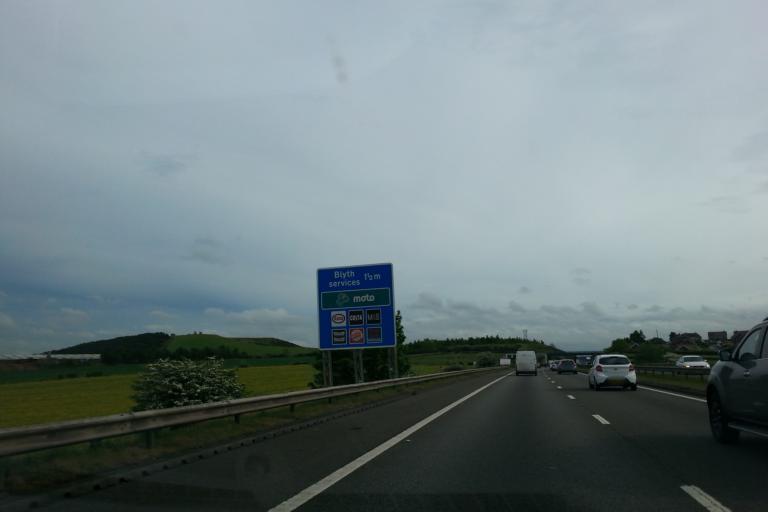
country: GB
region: England
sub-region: Doncaster
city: Tickhill
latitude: 53.4125
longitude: -1.0831
